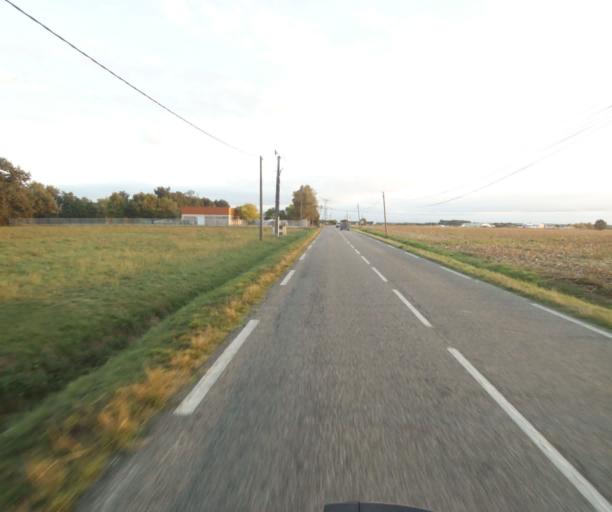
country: FR
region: Midi-Pyrenees
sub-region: Departement du Tarn-et-Garonne
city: Verdun-sur-Garonne
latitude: 43.8281
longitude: 1.2436
